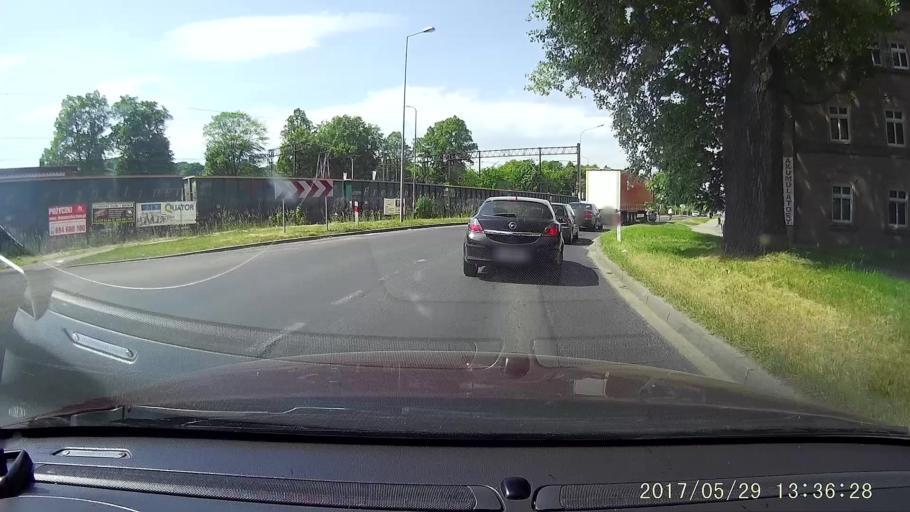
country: PL
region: Lower Silesian Voivodeship
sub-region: Powiat lubanski
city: Luban
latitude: 51.1121
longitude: 15.2943
